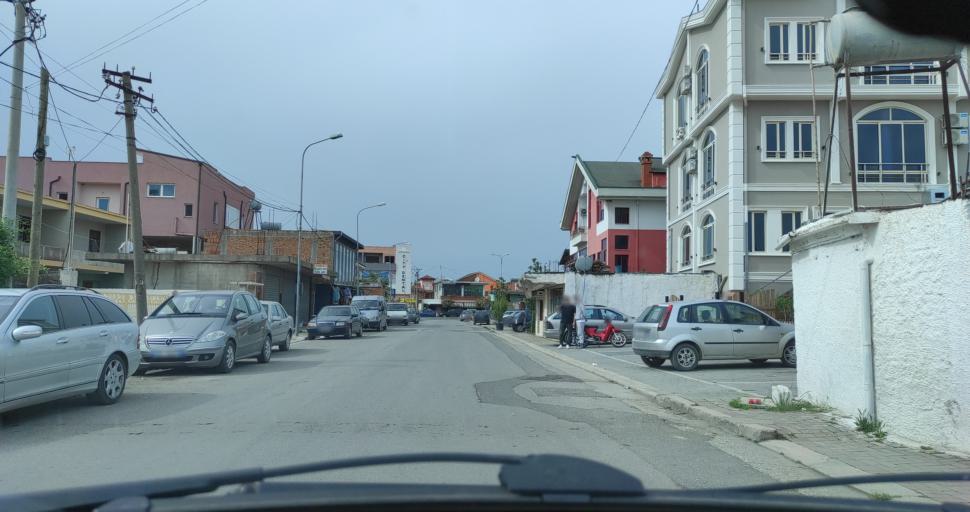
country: AL
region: Durres
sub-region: Rrethi i Krujes
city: Fushe-Kruje
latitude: 41.4778
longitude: 19.7176
